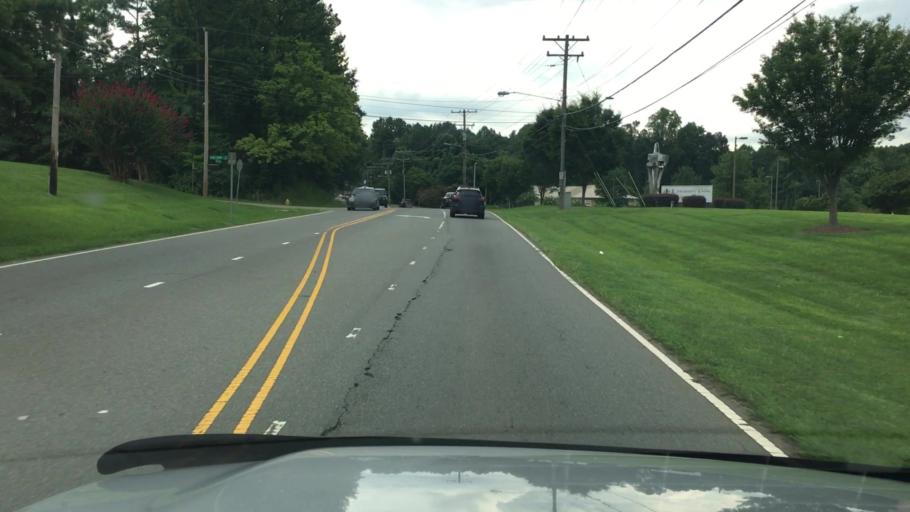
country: US
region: North Carolina
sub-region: Mecklenburg County
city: Charlotte
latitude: 35.3177
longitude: -80.8648
